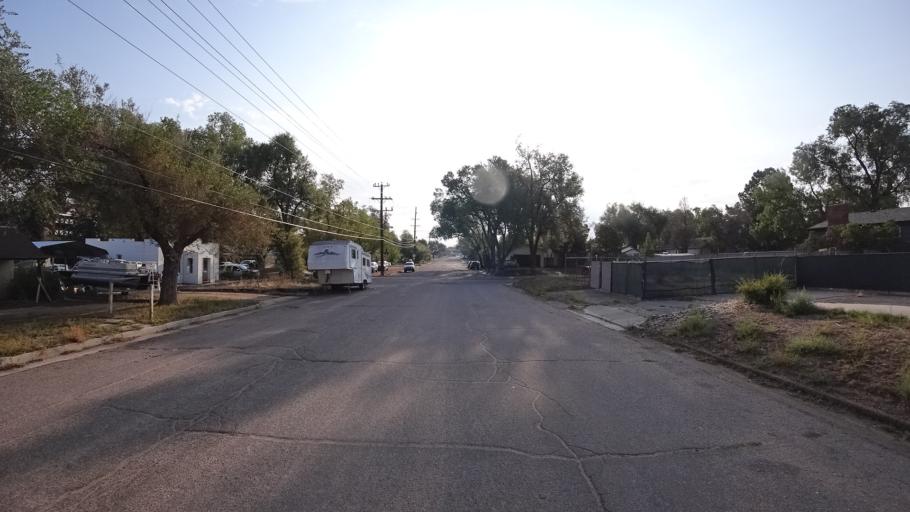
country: US
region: Colorado
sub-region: El Paso County
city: Colorado Springs
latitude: 38.8343
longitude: -104.7937
